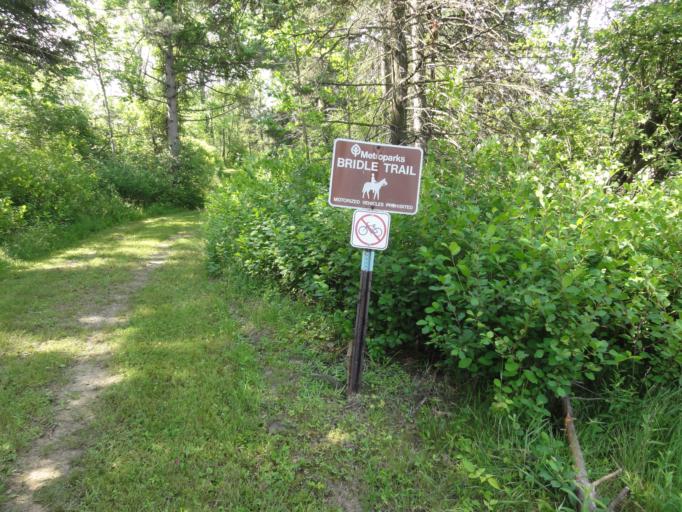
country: US
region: Ohio
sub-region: Cuyahoga County
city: Solon
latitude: 41.4020
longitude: -81.4763
